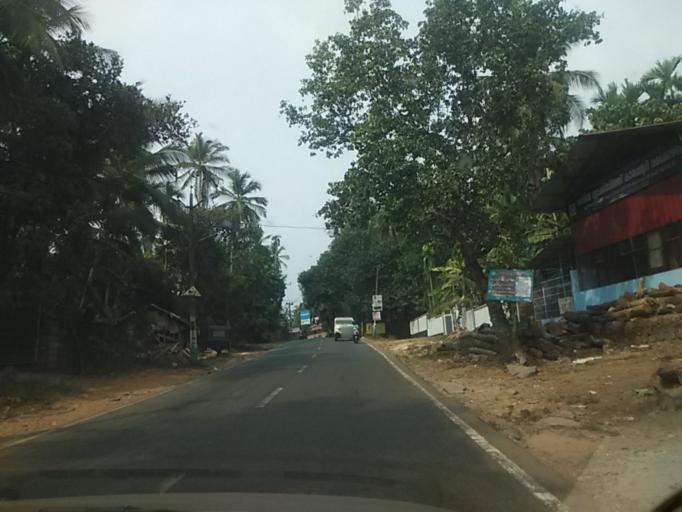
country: IN
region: Kerala
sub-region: Kozhikode
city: Naduvannur
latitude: 11.4712
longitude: 75.7738
